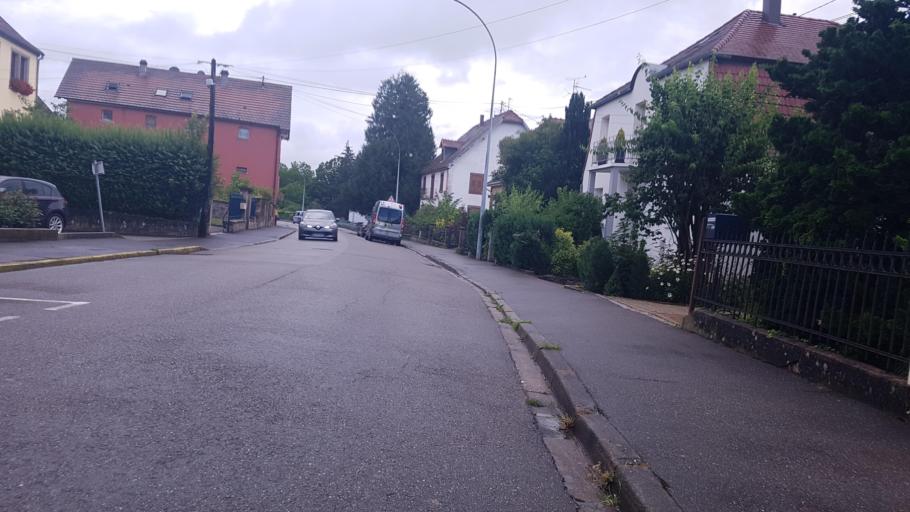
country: FR
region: Alsace
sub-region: Departement du Bas-Rhin
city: Saverne
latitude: 48.7366
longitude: 7.3633
